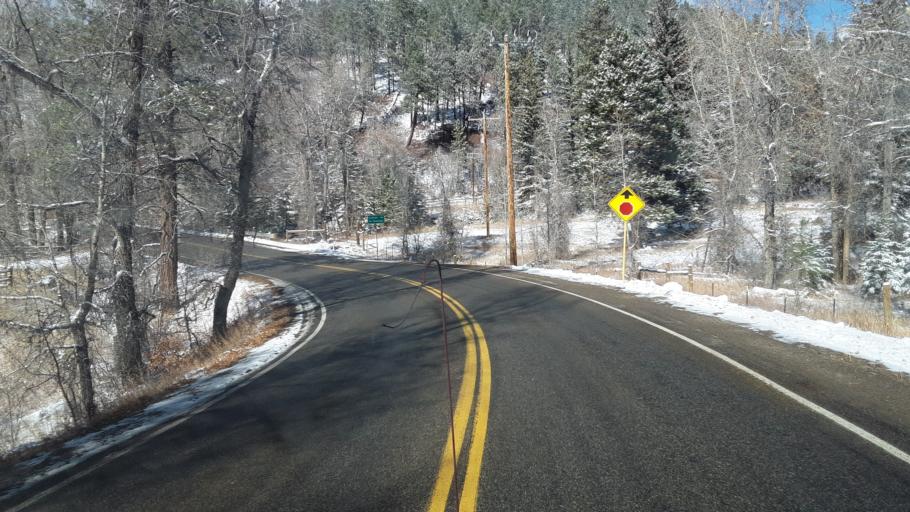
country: US
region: Colorado
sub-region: La Plata County
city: Bayfield
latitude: 37.3599
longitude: -107.6703
